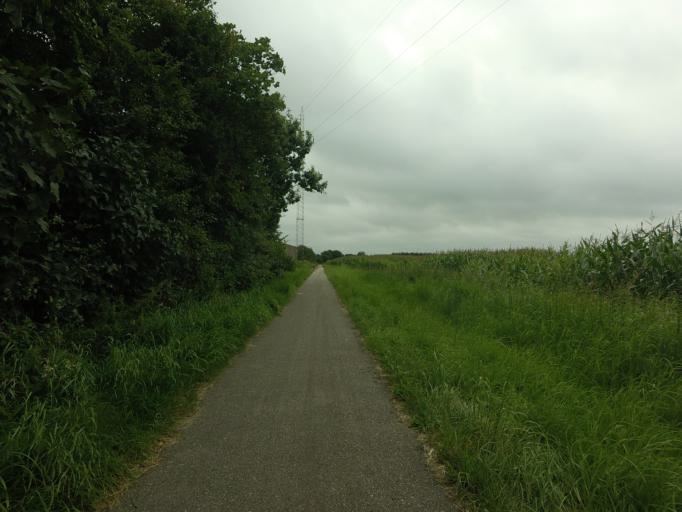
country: DK
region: Central Jutland
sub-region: Horsens Kommune
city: Braedstrup
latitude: 56.0024
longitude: 9.5885
